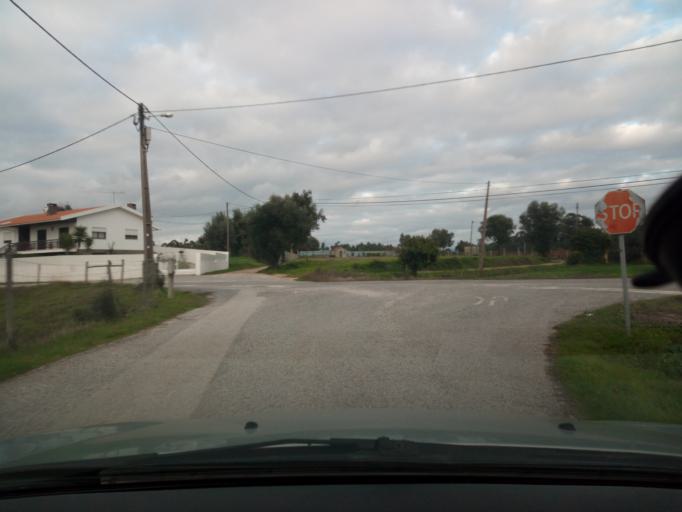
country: PT
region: Aveiro
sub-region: Oliveira do Bairro
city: Oliveira do Bairro
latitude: 40.5506
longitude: -8.4873
